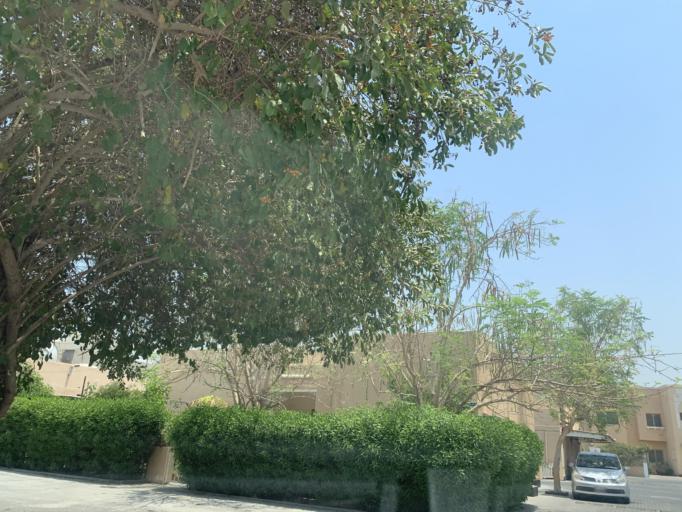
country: BH
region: Manama
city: Jidd Hafs
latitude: 26.2171
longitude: 50.5632
